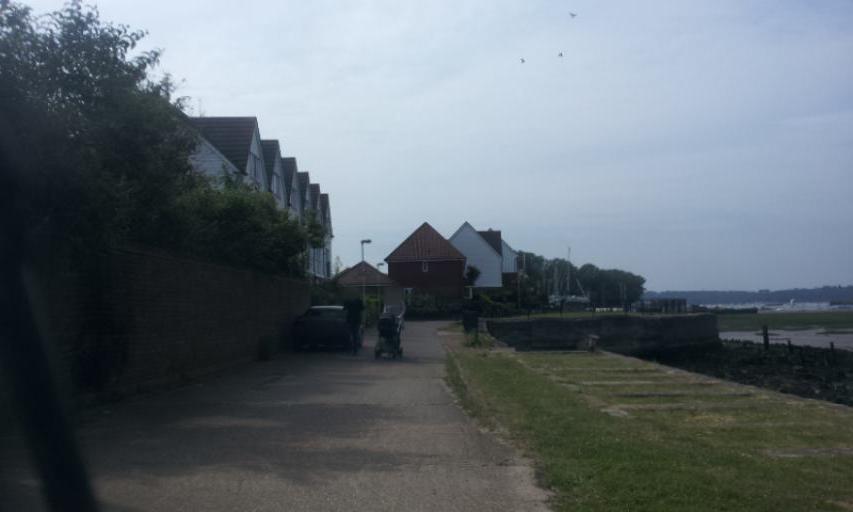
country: GB
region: England
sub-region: Kent
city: Gillingham
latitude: 51.3920
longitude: 0.5718
